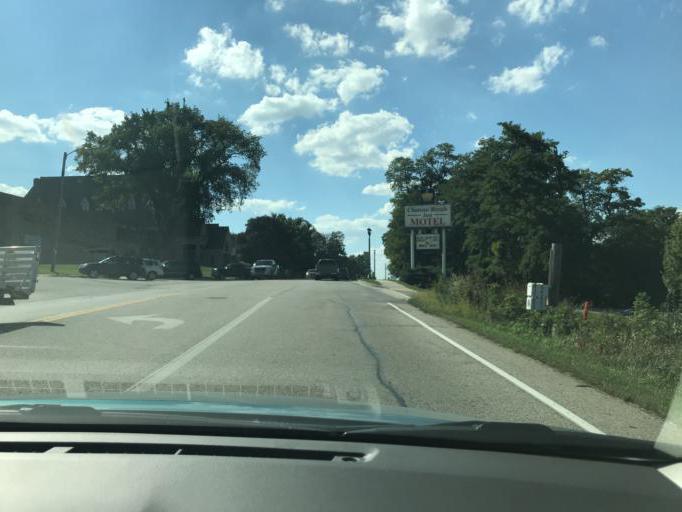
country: US
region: Wisconsin
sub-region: Walworth County
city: Lake Geneva
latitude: 42.5918
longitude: -88.4231
